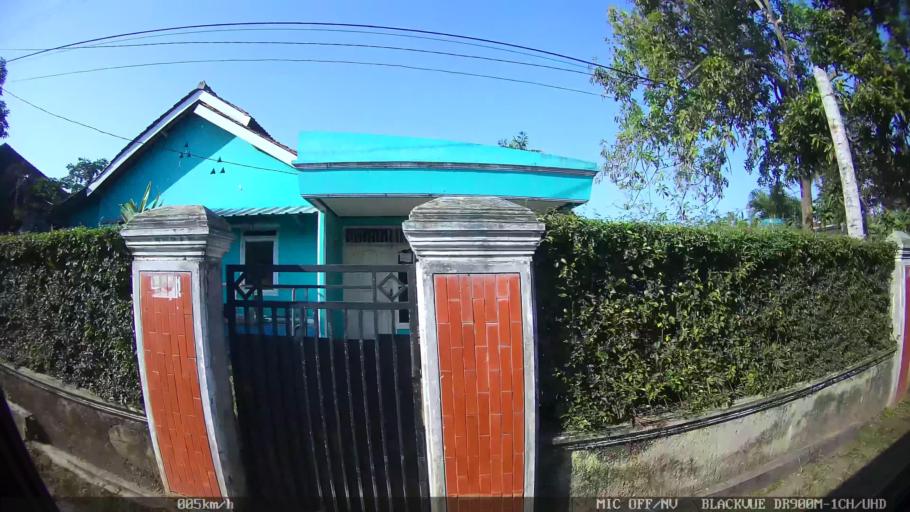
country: ID
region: Lampung
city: Kedaton
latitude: -5.3736
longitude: 105.2282
